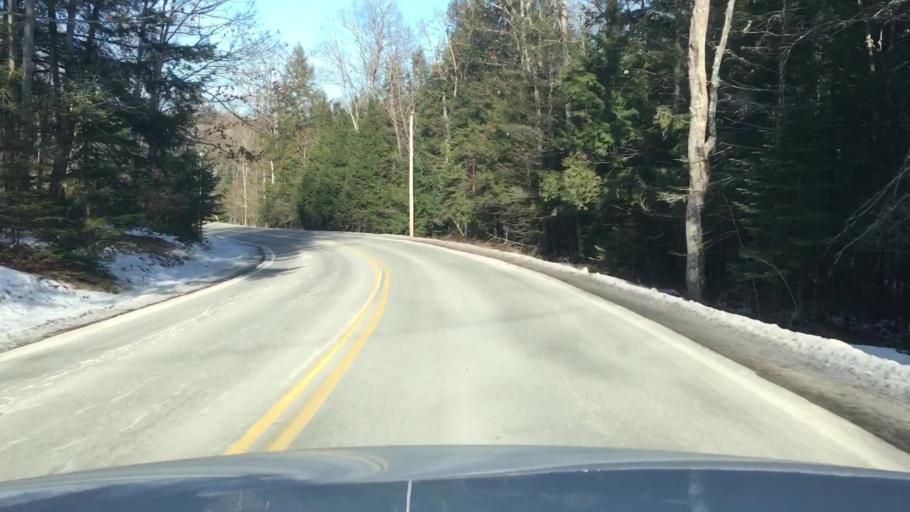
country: US
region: Maine
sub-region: Hancock County
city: Dedham
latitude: 44.6343
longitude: -68.6996
